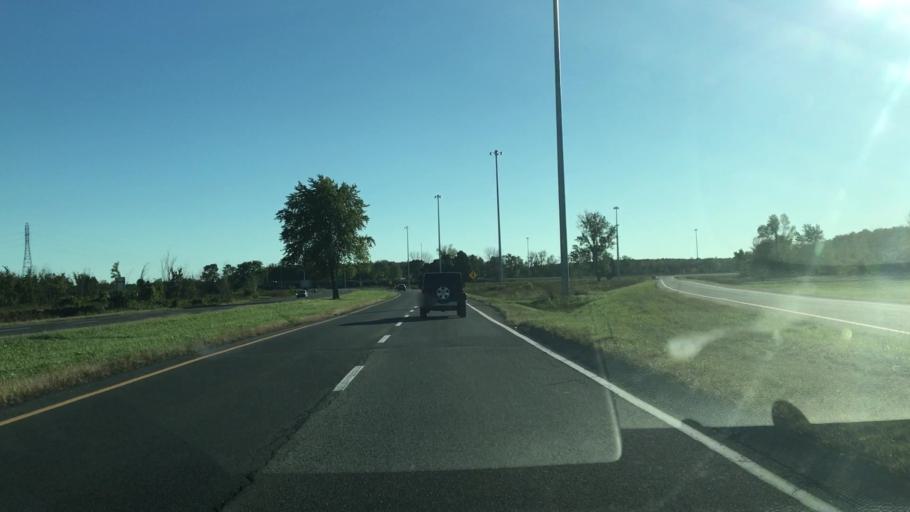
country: CA
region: Quebec
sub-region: Monteregie
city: Les Coteaux
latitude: 45.2802
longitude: -74.1933
